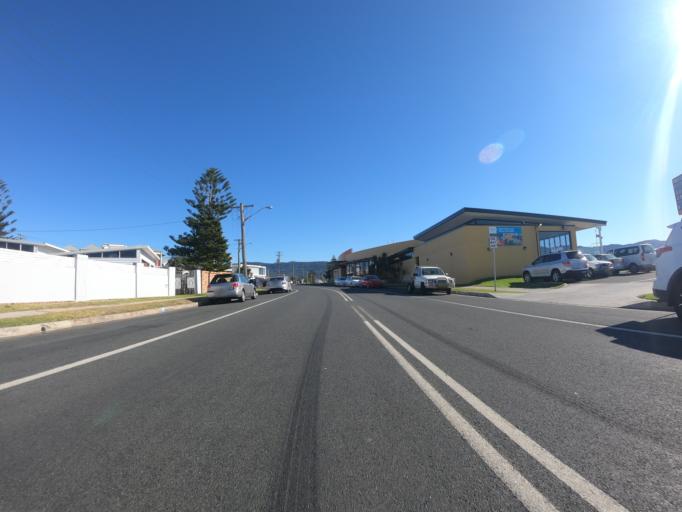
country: AU
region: New South Wales
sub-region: Wollongong
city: East Corrimal
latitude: -34.3854
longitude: 150.9143
